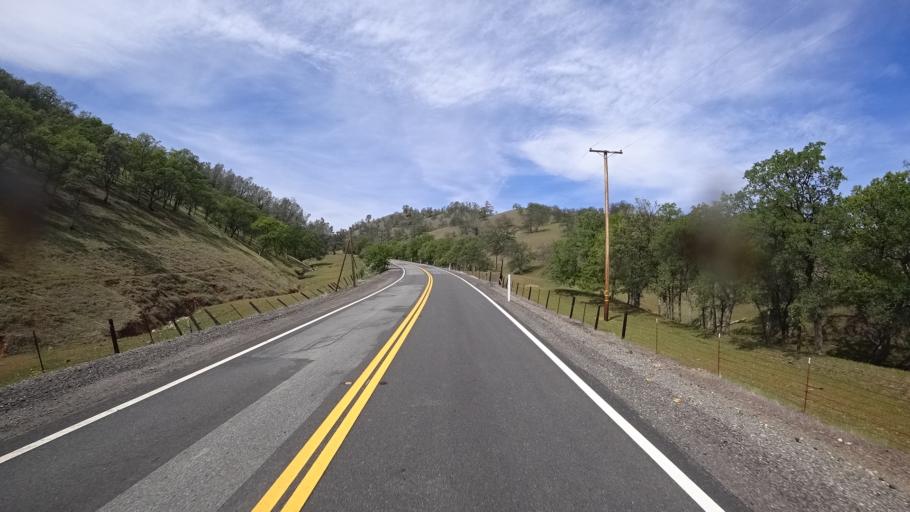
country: US
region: California
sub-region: Glenn County
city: Willows
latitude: 39.5982
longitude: -122.4950
